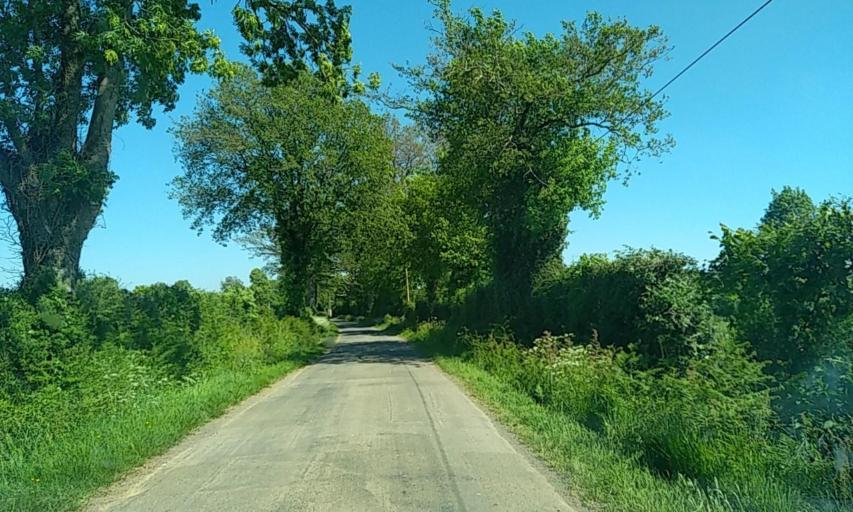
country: FR
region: Poitou-Charentes
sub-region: Departement des Deux-Sevres
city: Boisme
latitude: 46.7796
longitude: -0.4568
